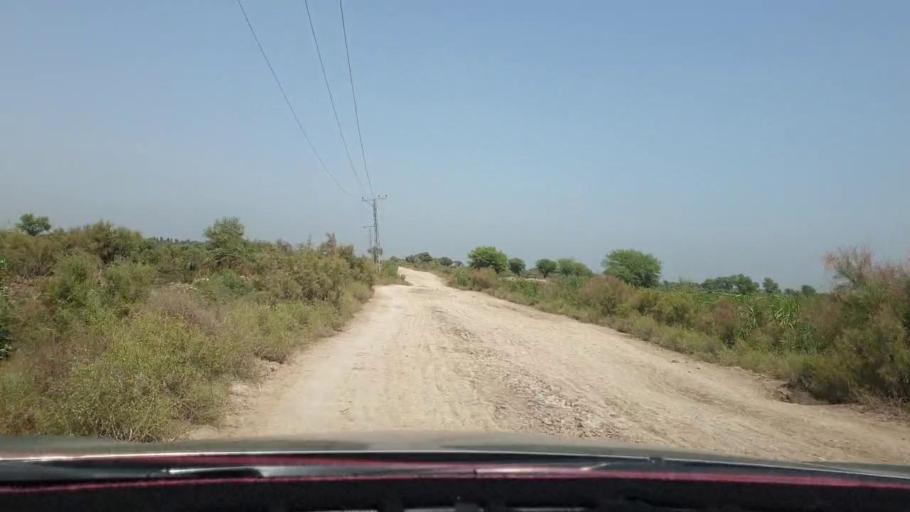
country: PK
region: Sindh
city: Warah
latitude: 27.3996
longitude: 67.6886
